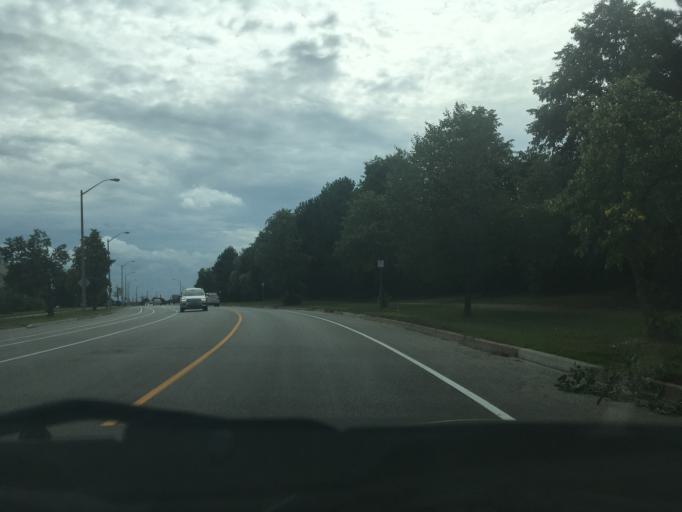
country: CA
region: Ontario
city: Brampton
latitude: 43.6642
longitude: -79.7245
